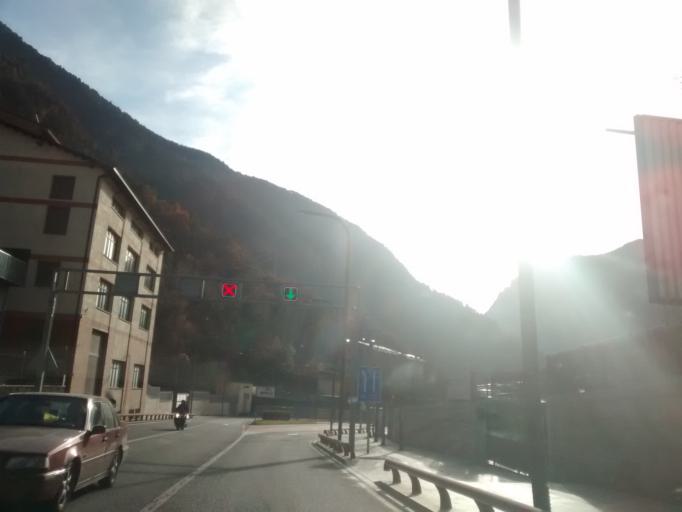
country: AD
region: Sant Julia de Loria
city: Sant Julia de Loria
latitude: 42.4906
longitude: 1.4963
